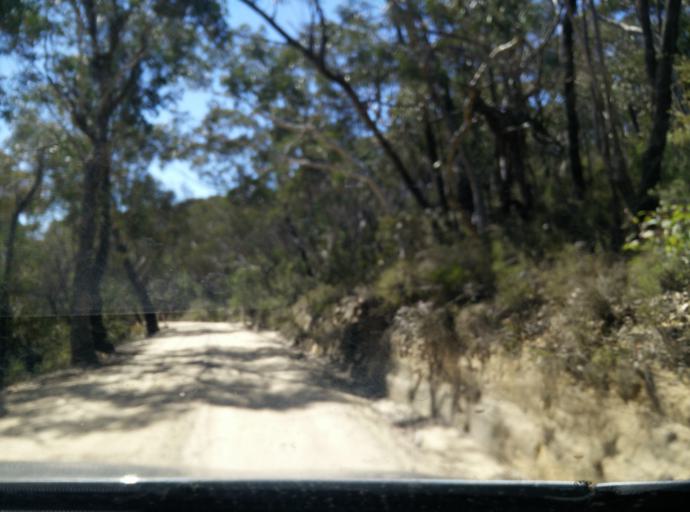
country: AU
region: New South Wales
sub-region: Blue Mountains Municipality
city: Blackheath
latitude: -33.5873
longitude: 150.2724
